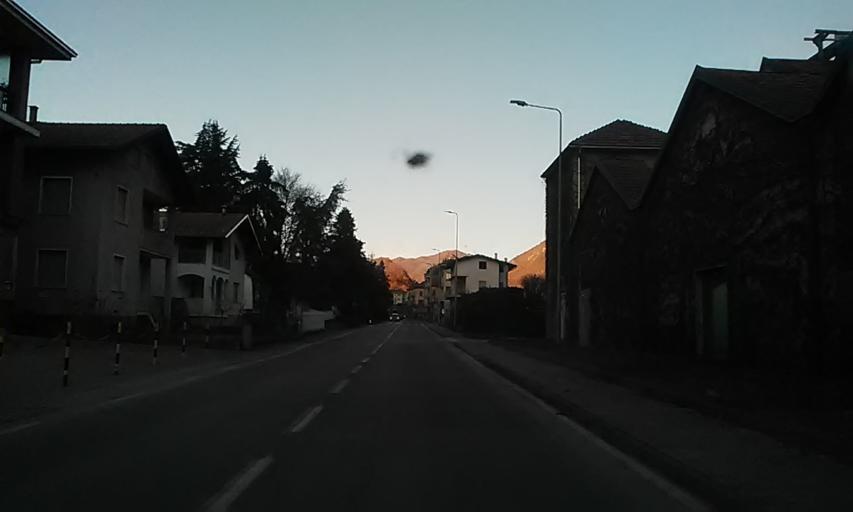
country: IT
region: Piedmont
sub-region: Provincia di Vercelli
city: Quarona
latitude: 45.7574
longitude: 8.2676
